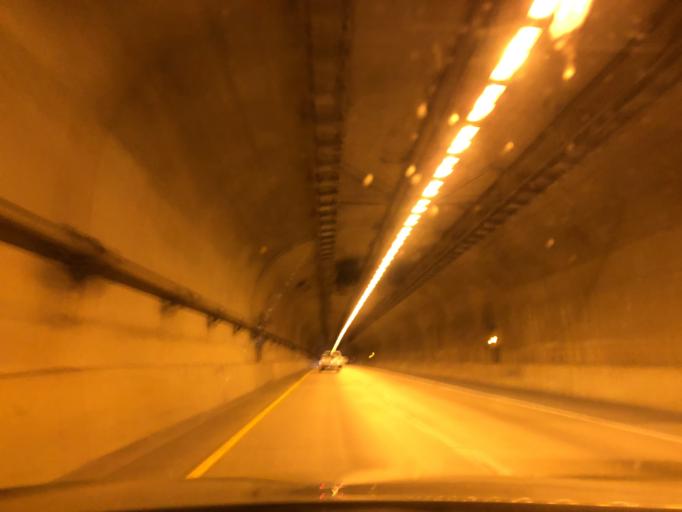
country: US
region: Arkansas
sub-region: Washington County
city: West Fork
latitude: 35.7700
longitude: -94.1880
